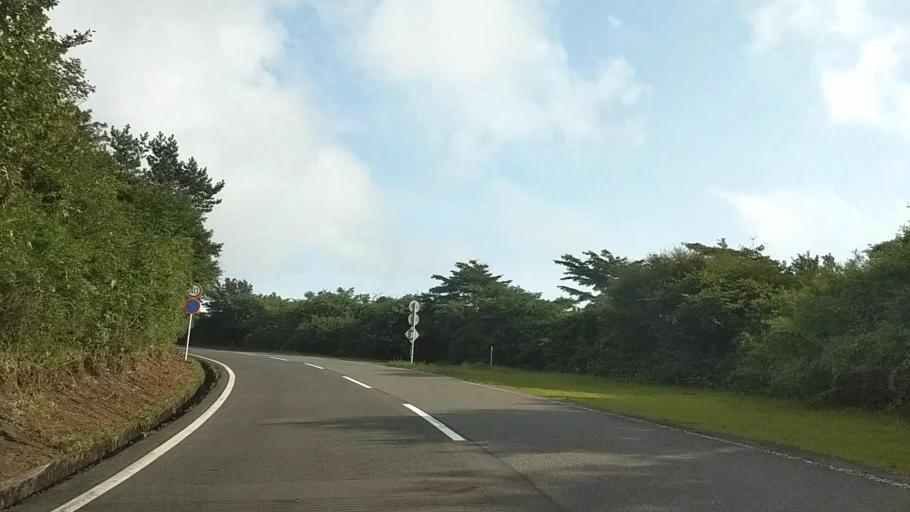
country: JP
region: Kanagawa
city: Hakone
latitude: 35.1885
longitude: 139.0019
